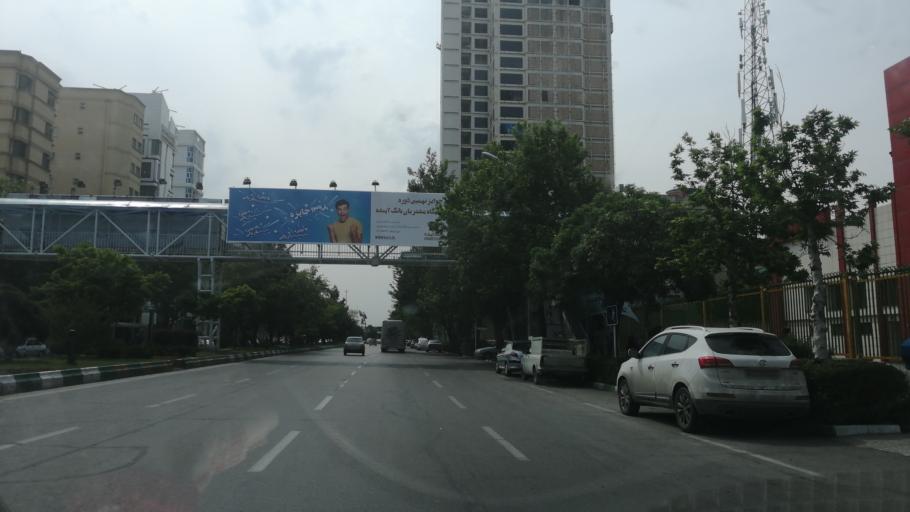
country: IR
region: Razavi Khorasan
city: Mashhad
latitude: 36.3244
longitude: 59.5673
